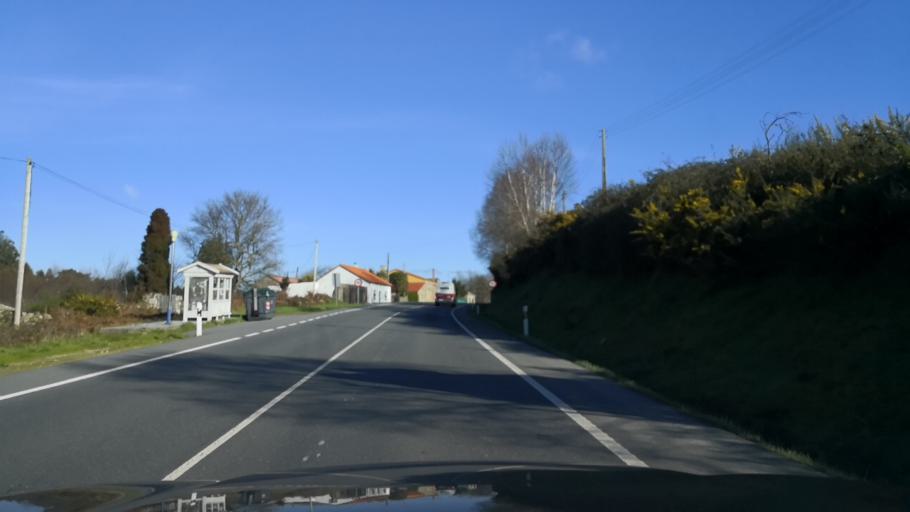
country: ES
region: Galicia
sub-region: Provincia de Pontevedra
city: Silleda
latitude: 42.7223
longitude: -8.2904
